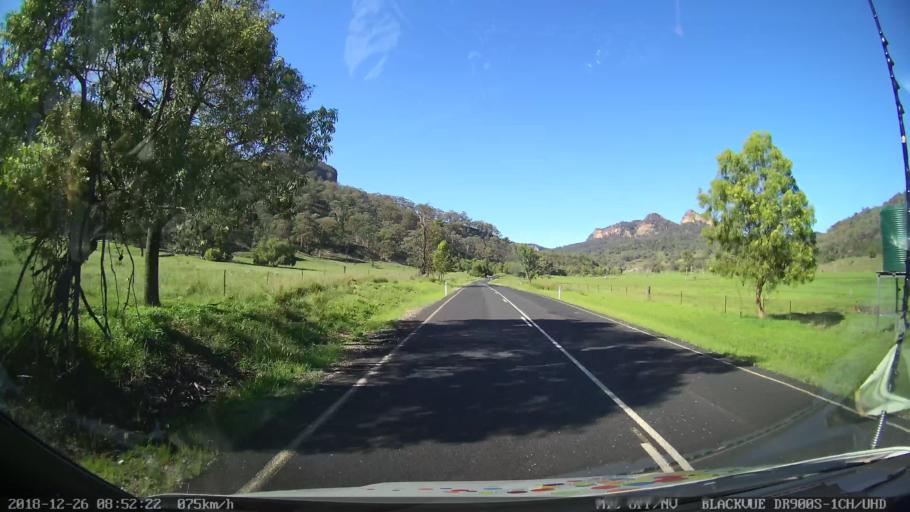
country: AU
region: New South Wales
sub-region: Mid-Western Regional
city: Kandos
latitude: -32.5959
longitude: 150.0865
